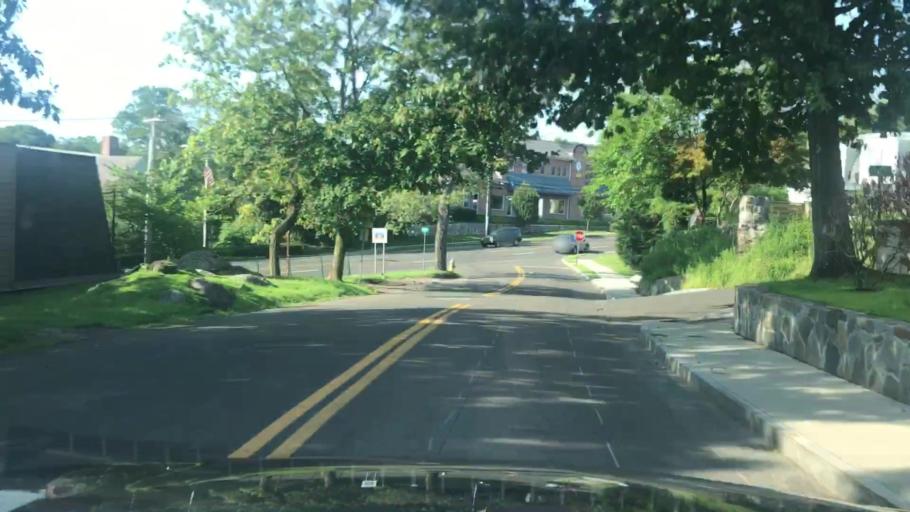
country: US
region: Connecticut
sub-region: Fairfield County
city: Greenwich
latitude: 41.0191
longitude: -73.6436
